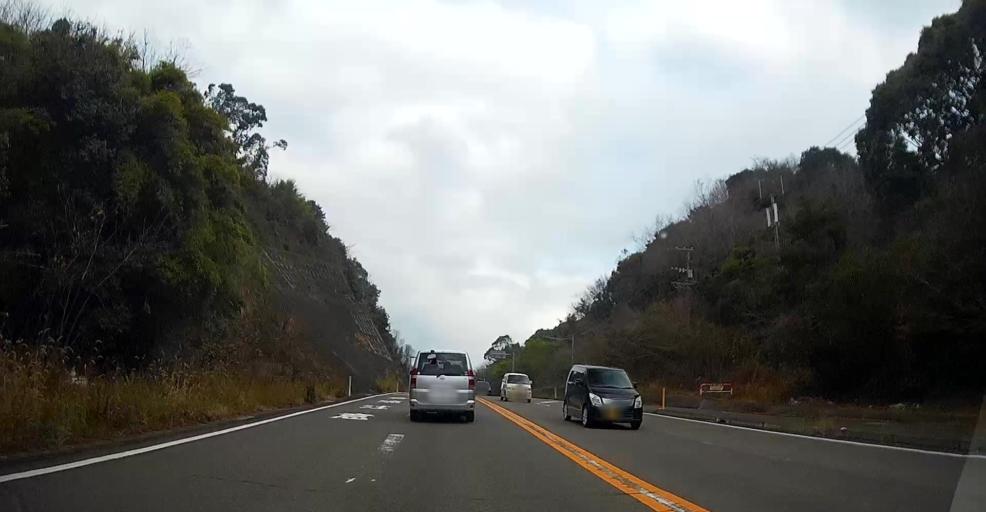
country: JP
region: Kumamoto
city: Yatsushiro
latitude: 32.5581
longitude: 130.4153
